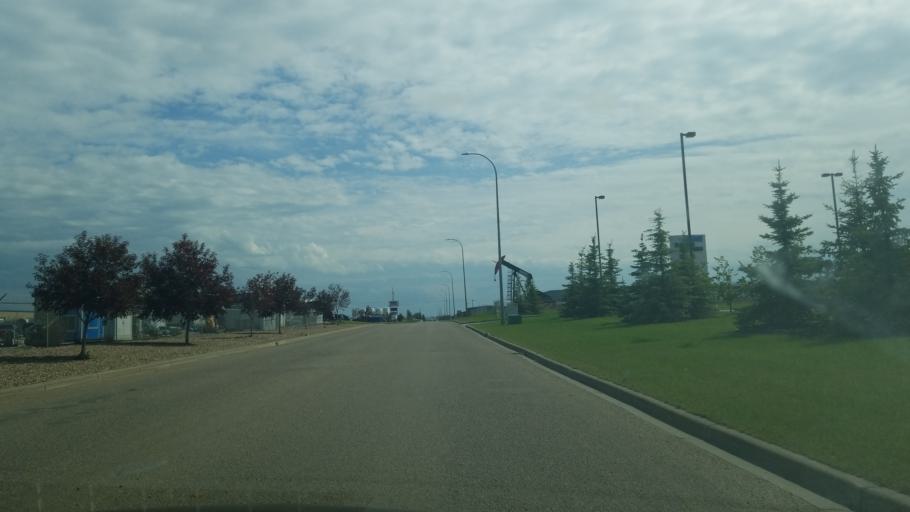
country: CA
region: Saskatchewan
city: Lloydminster
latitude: 53.2961
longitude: -110.0368
